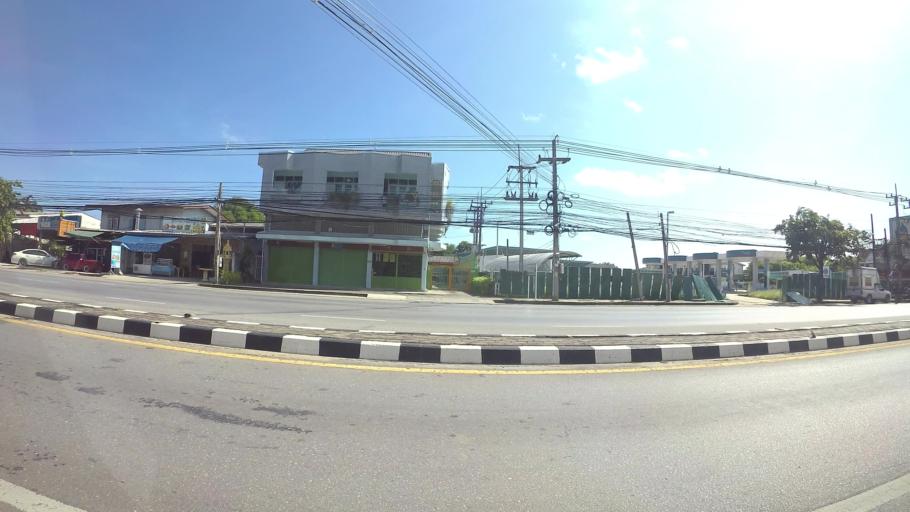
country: TH
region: Rayong
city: Rayong
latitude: 12.6729
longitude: 101.2943
